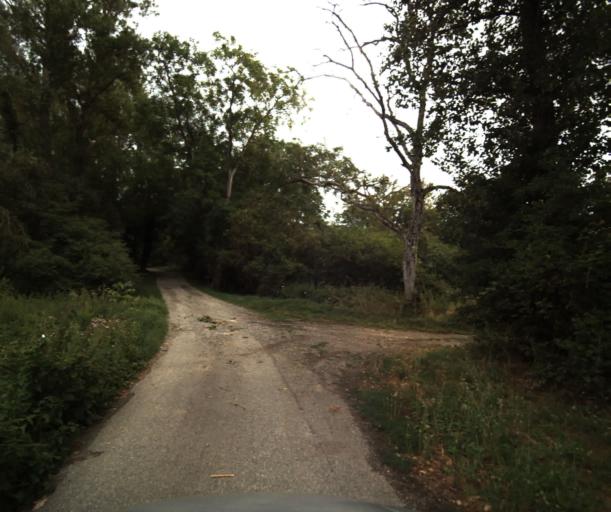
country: FR
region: Midi-Pyrenees
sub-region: Departement de la Haute-Garonne
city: Le Fauga
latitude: 43.4072
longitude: 1.3089
